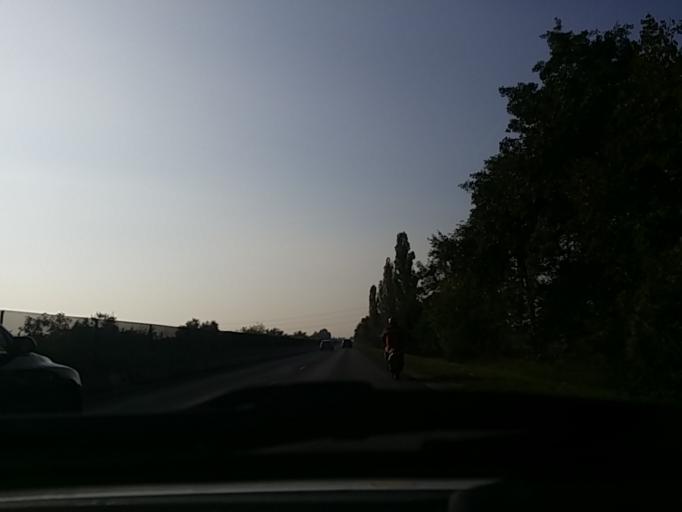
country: HU
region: Pest
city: Budakalasz
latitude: 47.6393
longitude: 19.0687
